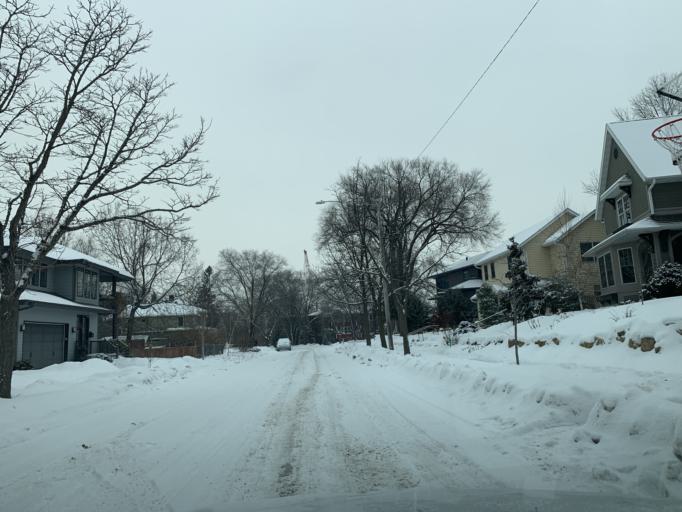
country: US
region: Minnesota
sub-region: Hennepin County
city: Saint Louis Park
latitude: 44.9515
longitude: -93.3227
